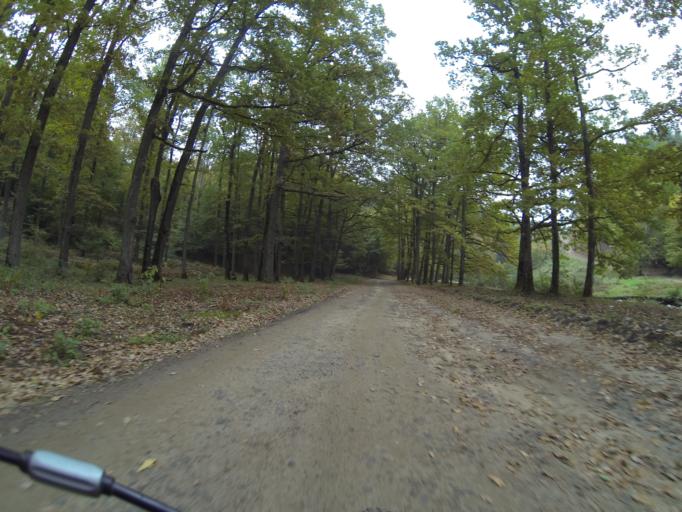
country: RO
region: Gorj
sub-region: Comuna Tismana
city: Sohodol
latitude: 45.0628
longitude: 22.8945
